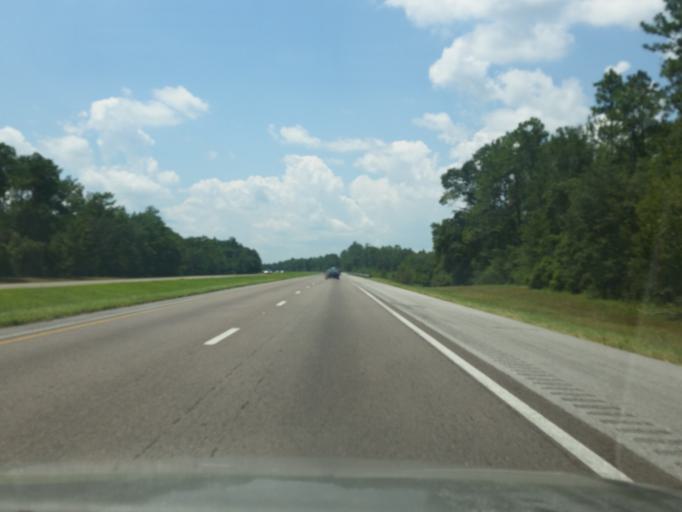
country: US
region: Alabama
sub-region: Baldwin County
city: Robertsdale
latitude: 30.6105
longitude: -87.5672
